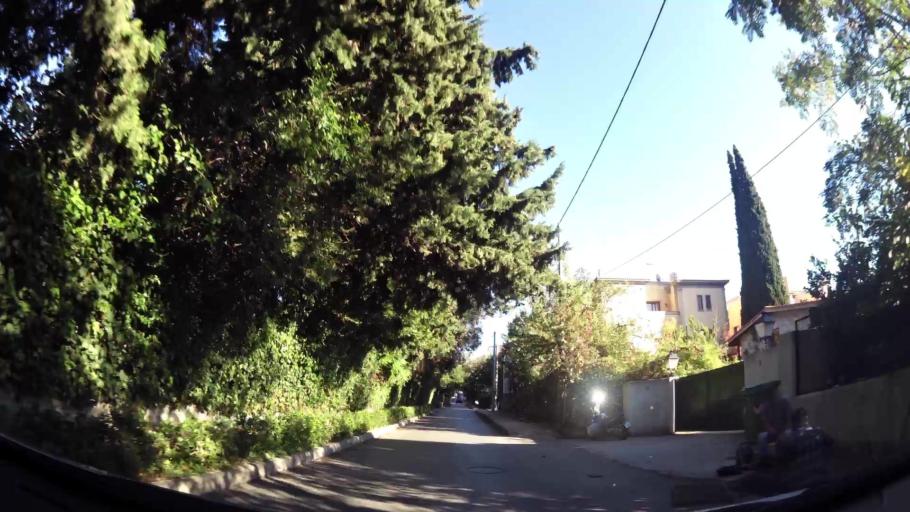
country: GR
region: Attica
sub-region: Nomarchia Athinas
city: Kifisia
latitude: 38.0843
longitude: 23.8042
